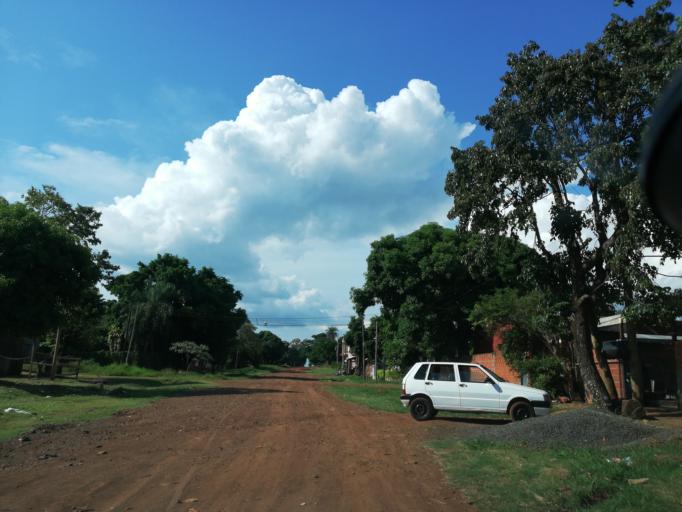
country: AR
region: Misiones
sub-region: Departamento de Capital
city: Posadas
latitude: -27.3906
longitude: -55.9236
